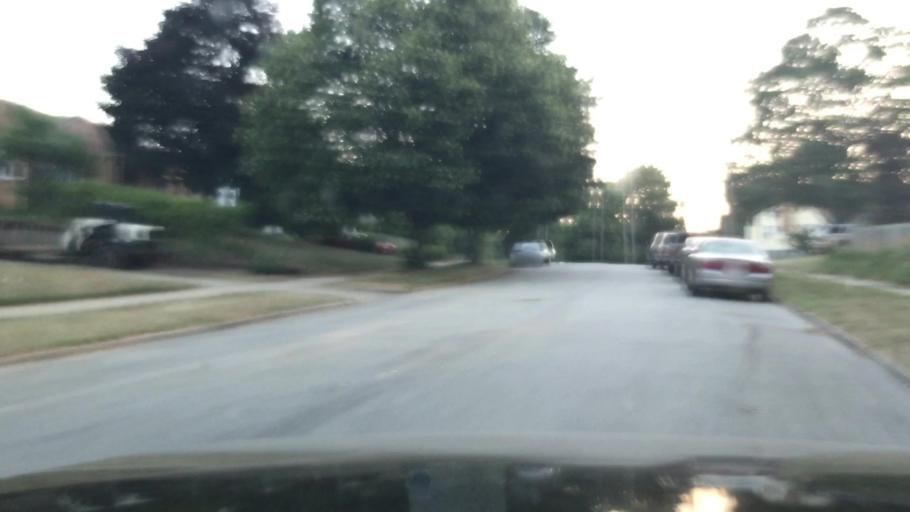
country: US
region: Michigan
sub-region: Kent County
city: Grand Rapids
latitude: 42.9669
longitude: -85.7095
